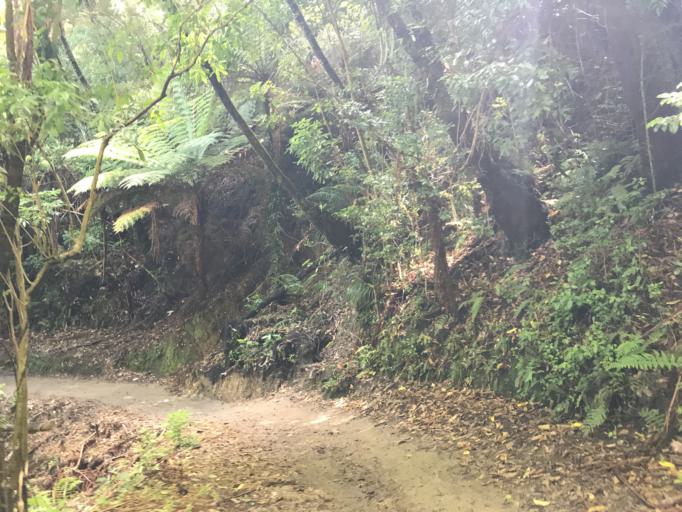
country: NZ
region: Marlborough
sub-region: Marlborough District
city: Picton
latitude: -41.2633
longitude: 173.9265
